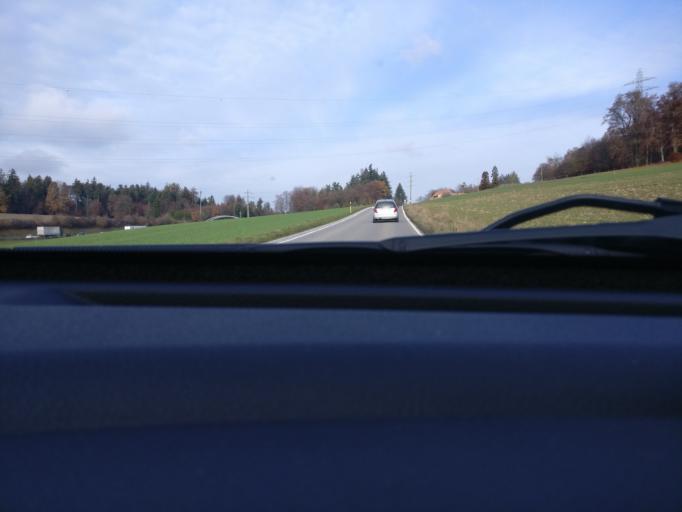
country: CH
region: Bern
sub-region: Bern-Mittelland District
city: Bolligen
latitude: 46.9908
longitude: 7.4827
